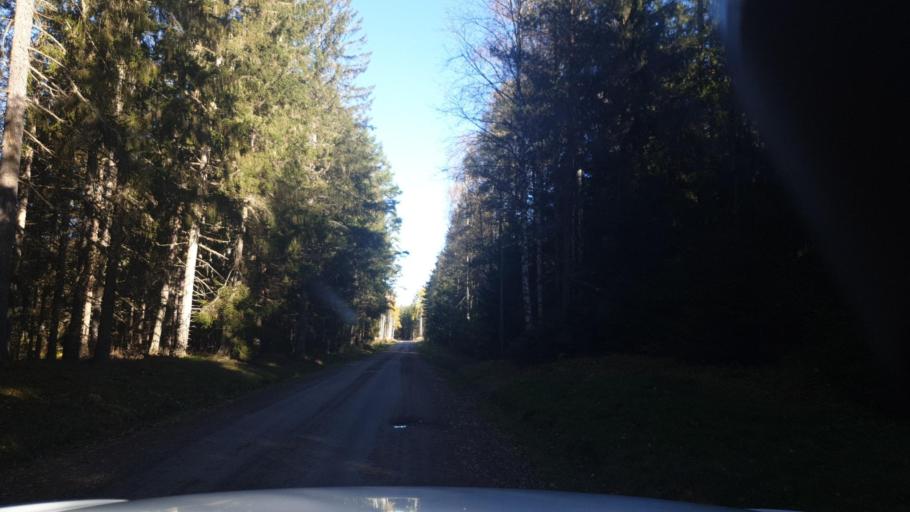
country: SE
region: Vaermland
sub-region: Arvika Kommun
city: Arvika
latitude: 59.5138
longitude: 12.7330
